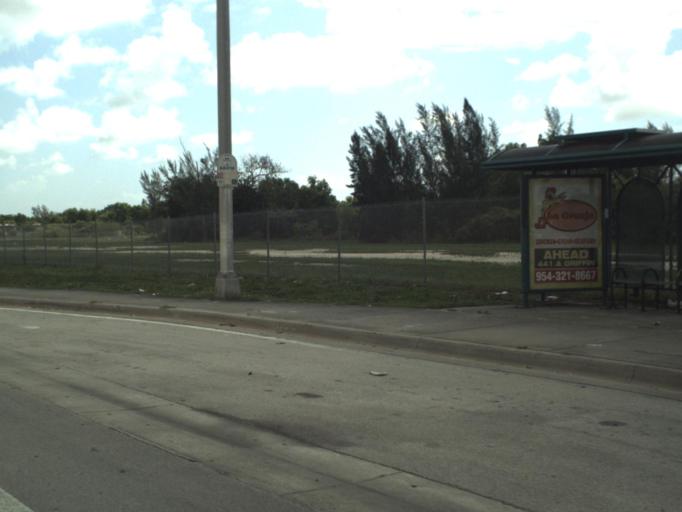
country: US
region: Florida
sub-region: Broward County
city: Davie
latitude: 26.0488
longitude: -80.2086
